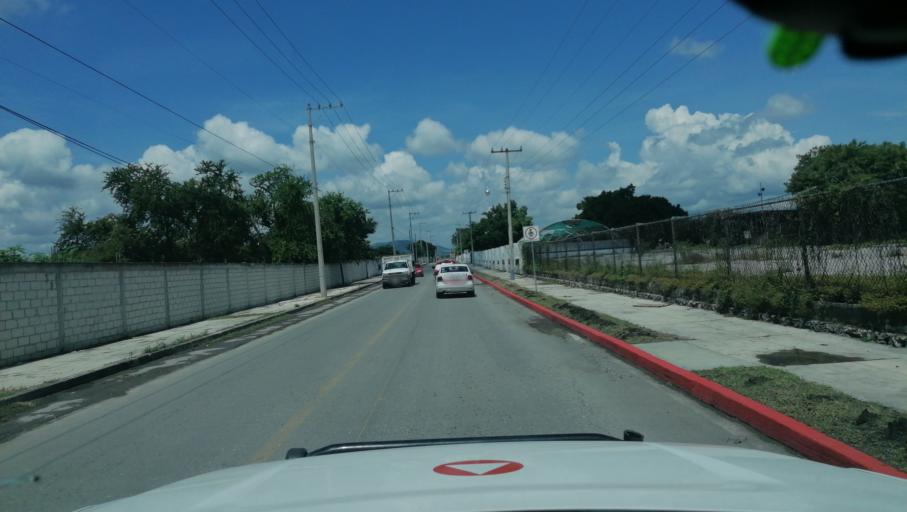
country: MX
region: Morelos
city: Zacatepec
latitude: 18.6495
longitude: -99.1842
